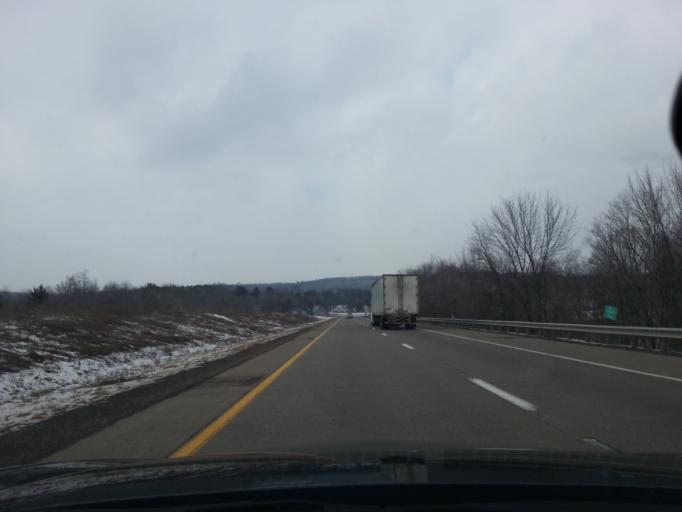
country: US
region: Pennsylvania
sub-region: Luzerne County
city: Conyngham
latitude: 41.0367
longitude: -76.0133
